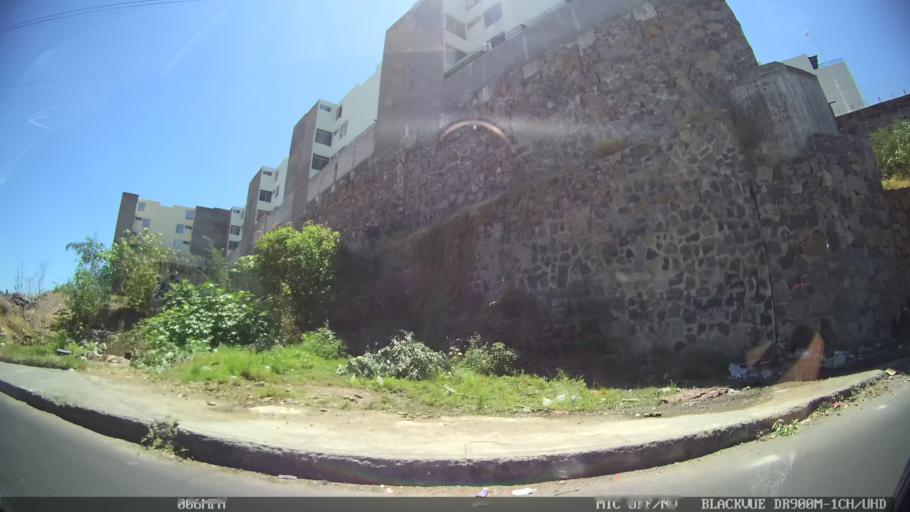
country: MX
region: Jalisco
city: Tlaquepaque
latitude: 20.6835
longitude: -103.2898
